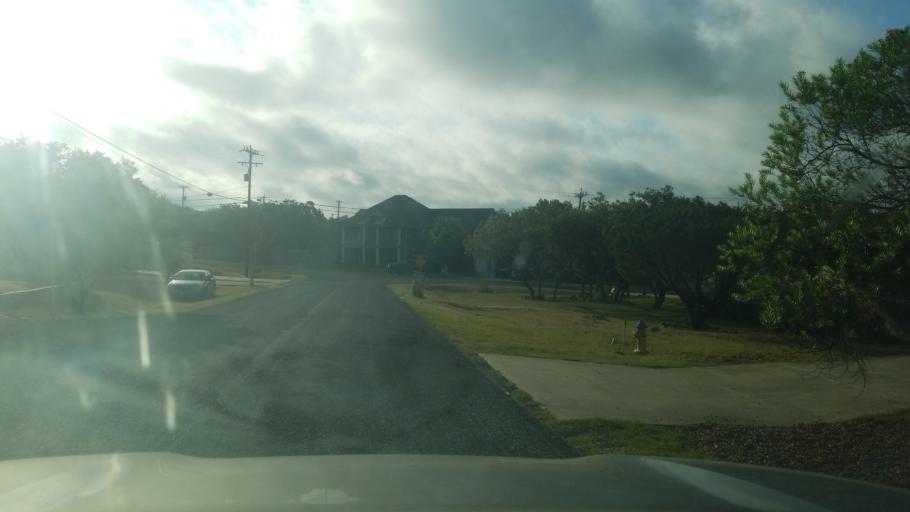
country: US
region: Texas
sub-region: Bexar County
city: Timberwood Park
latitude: 29.7003
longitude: -98.5016
